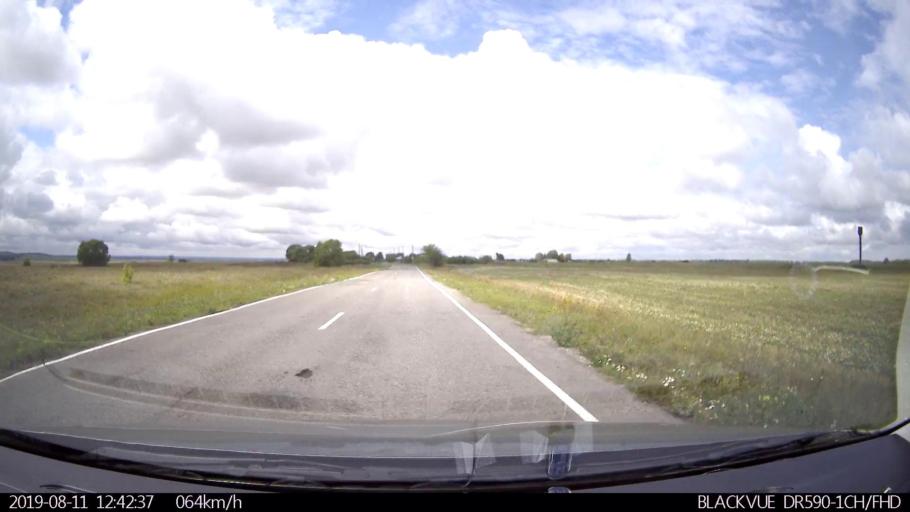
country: RU
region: Ulyanovsk
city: Ignatovka
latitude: 53.8471
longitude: 47.7495
